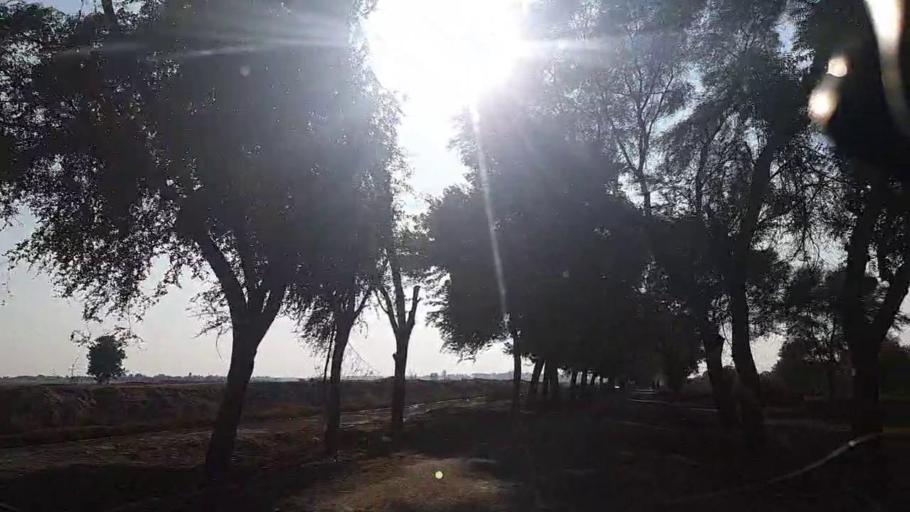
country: PK
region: Sindh
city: Khanpur
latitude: 27.6421
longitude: 69.6012
